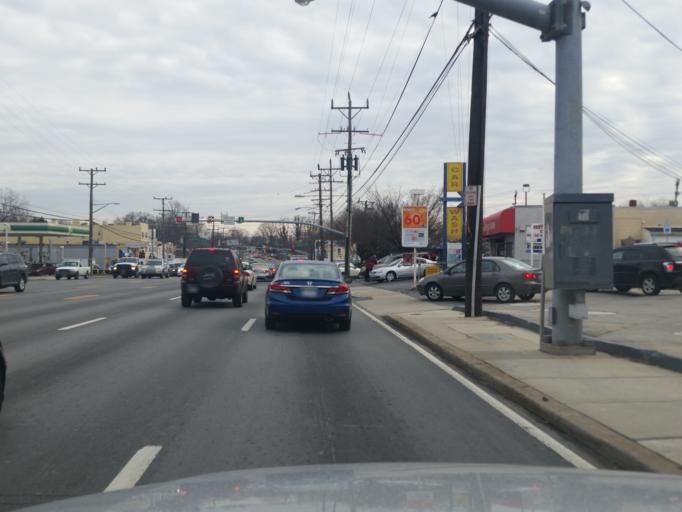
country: US
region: Maryland
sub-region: Montgomery County
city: Forest Glen
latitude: 39.0107
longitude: -77.0411
